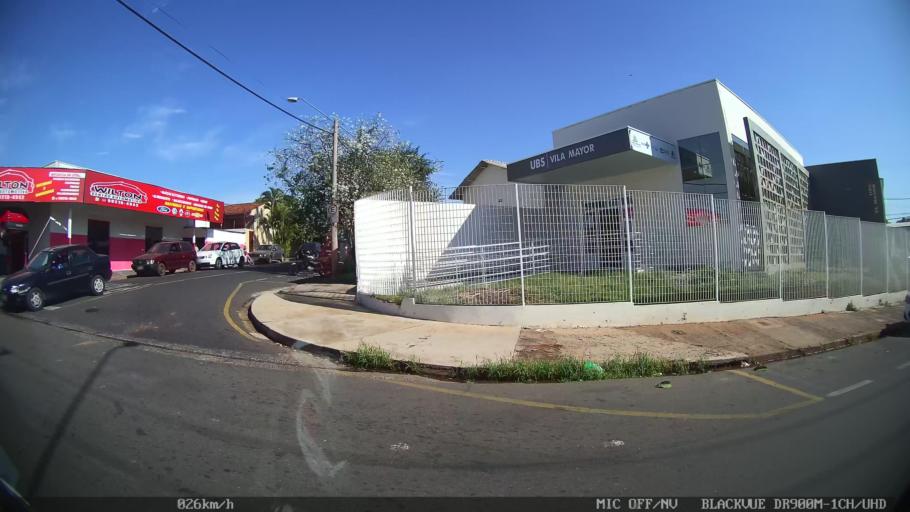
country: BR
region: Sao Paulo
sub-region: Sao Jose Do Rio Preto
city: Sao Jose do Rio Preto
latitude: -20.7817
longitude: -49.3867
